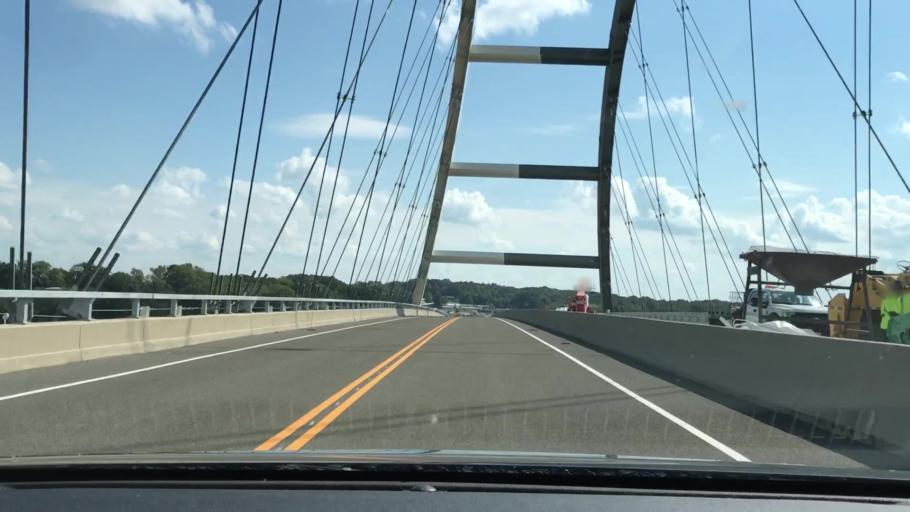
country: US
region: Kentucky
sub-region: Trigg County
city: Cadiz
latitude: 36.8000
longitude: -87.9762
